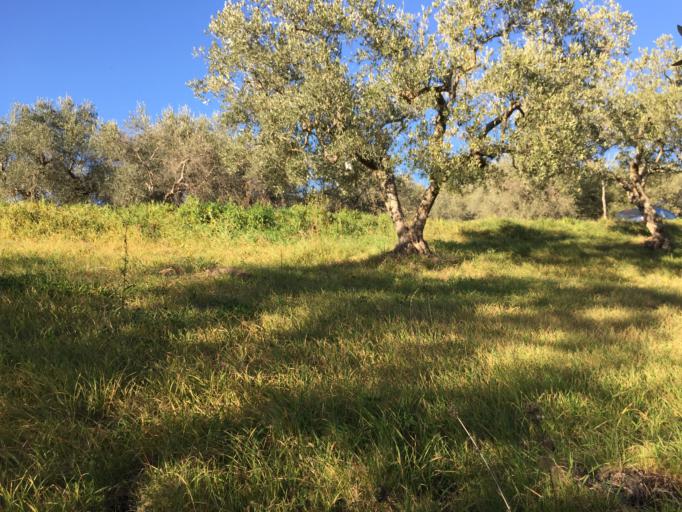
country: IT
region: Campania
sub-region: Provincia di Salerno
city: Salvitelle
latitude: 40.6017
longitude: 15.4805
